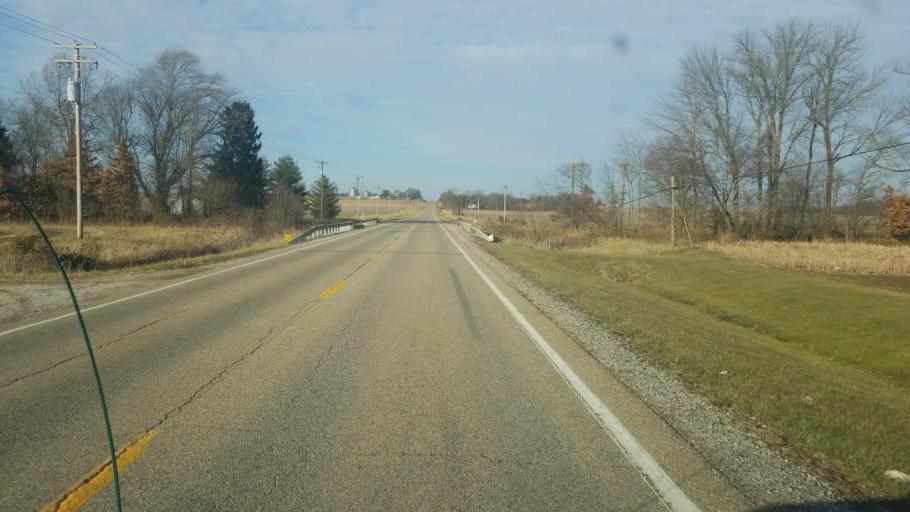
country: US
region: Illinois
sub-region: Lawrence County
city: Lawrenceville
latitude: 38.6464
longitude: -87.6943
